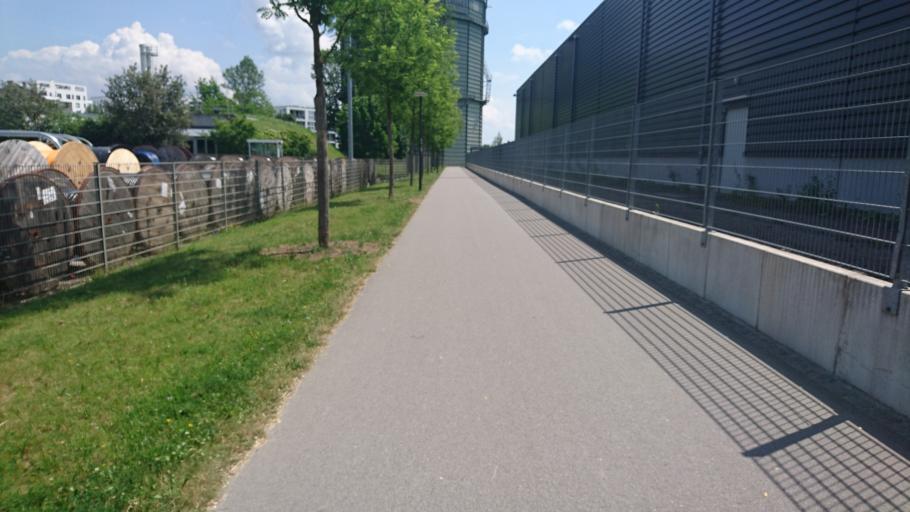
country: DE
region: Bavaria
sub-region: Upper Palatinate
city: Regensburg
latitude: 49.0124
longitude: 12.1193
